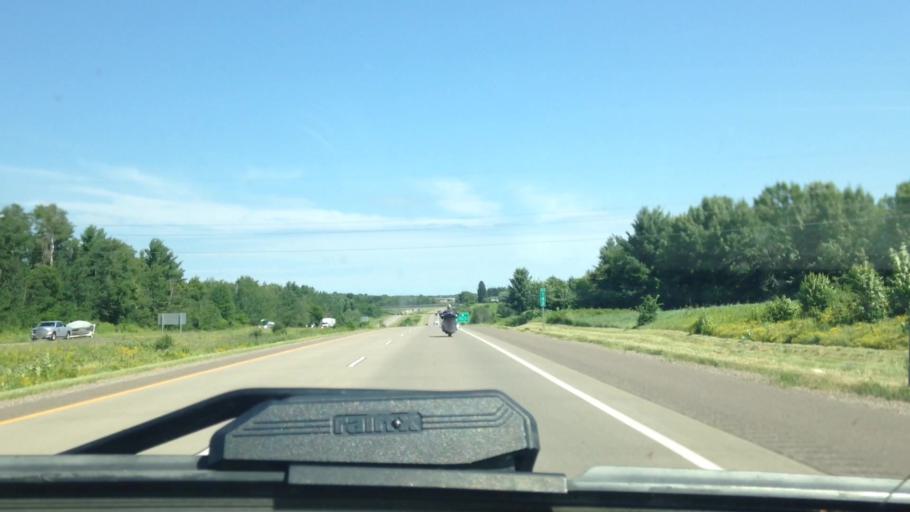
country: US
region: Wisconsin
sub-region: Barron County
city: Rice Lake
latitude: 45.4869
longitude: -91.7619
